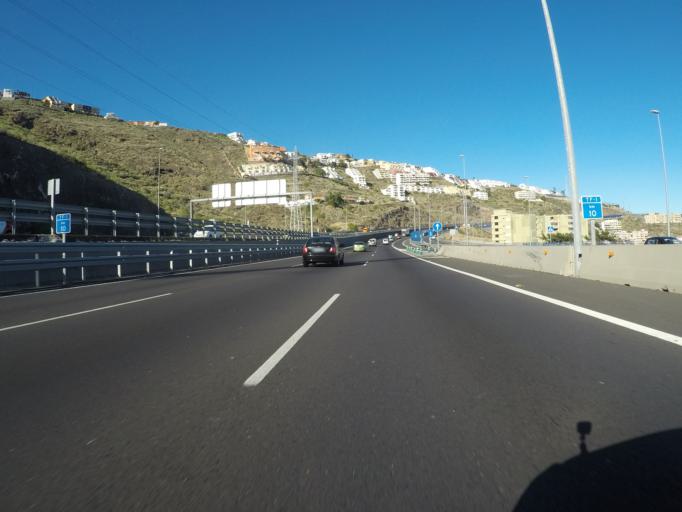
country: ES
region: Canary Islands
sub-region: Provincia de Santa Cruz de Tenerife
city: Candelaria
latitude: 28.4039
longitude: -16.3361
